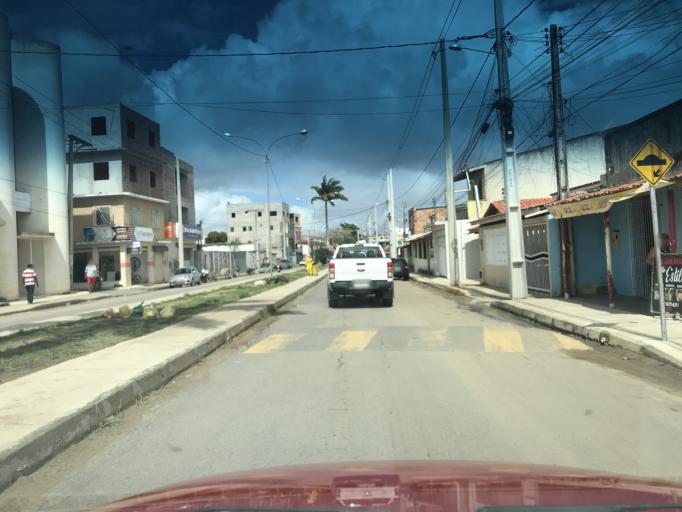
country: BR
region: Bahia
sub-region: Santo Antonio De Jesus
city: Santo Antonio de Jesus
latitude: -12.9774
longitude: -39.2753
